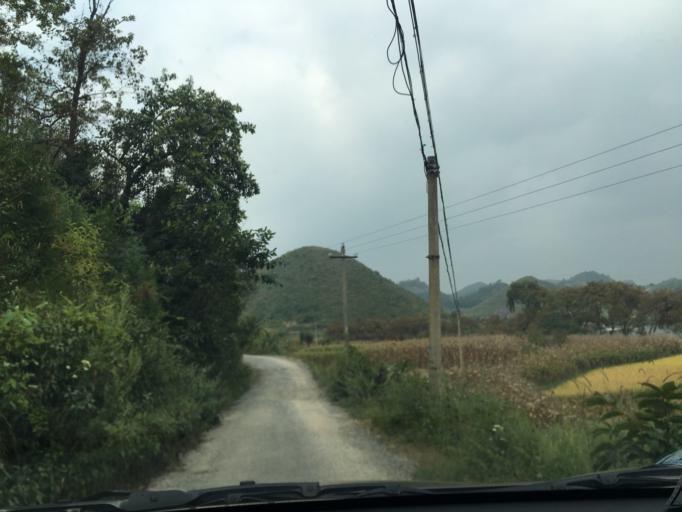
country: CN
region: Guizhou Sheng
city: Anshun
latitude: 25.5735
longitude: 105.6304
